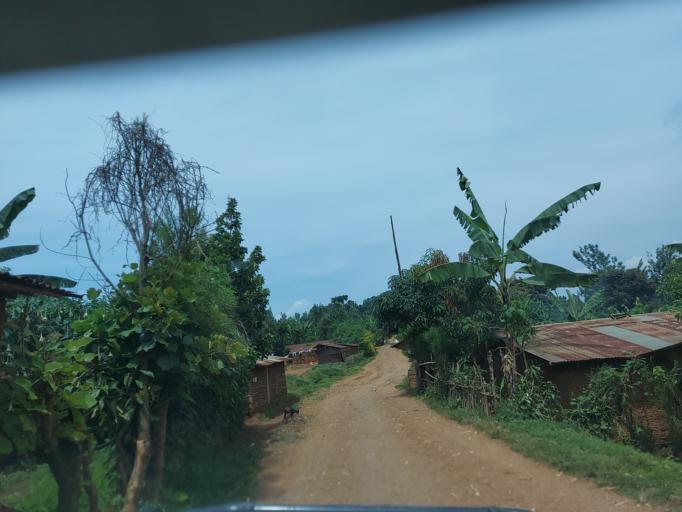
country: CD
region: South Kivu
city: Bukavu
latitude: -2.2346
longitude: 28.8496
